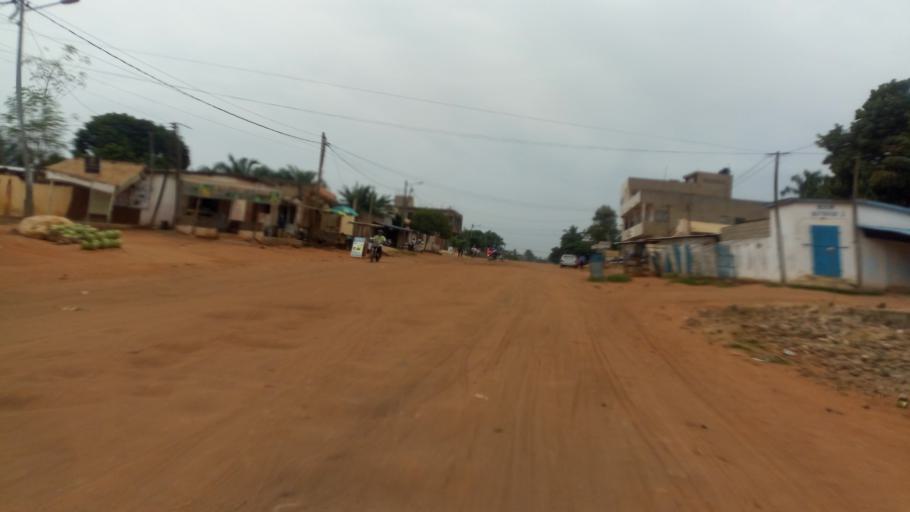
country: TG
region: Maritime
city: Lome
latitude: 6.1808
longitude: 1.1752
